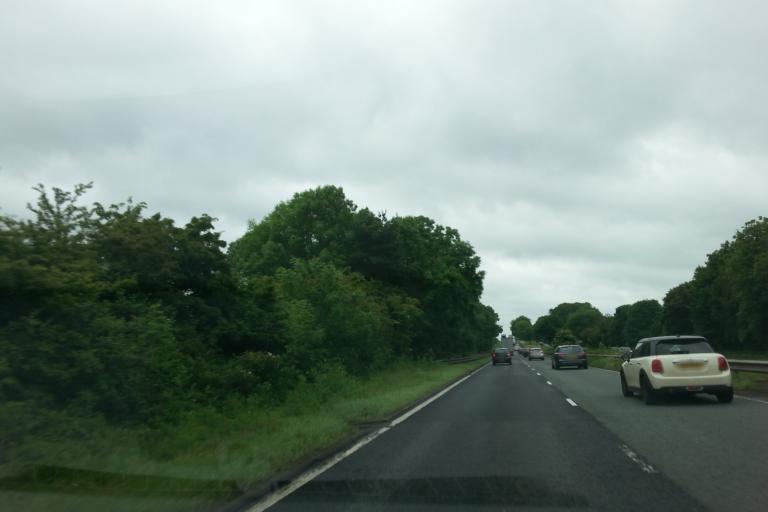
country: GB
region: England
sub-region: District of Rutland
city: Greetham
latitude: 52.7355
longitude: -0.6004
